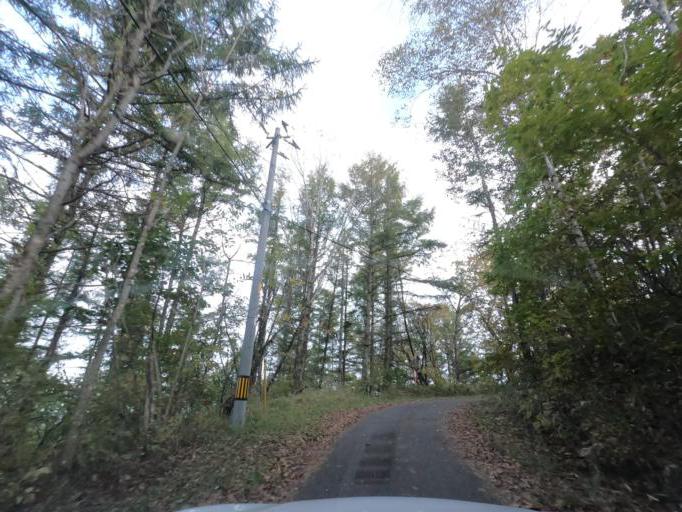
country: JP
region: Hokkaido
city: Obihiro
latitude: 42.5840
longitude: 143.3144
